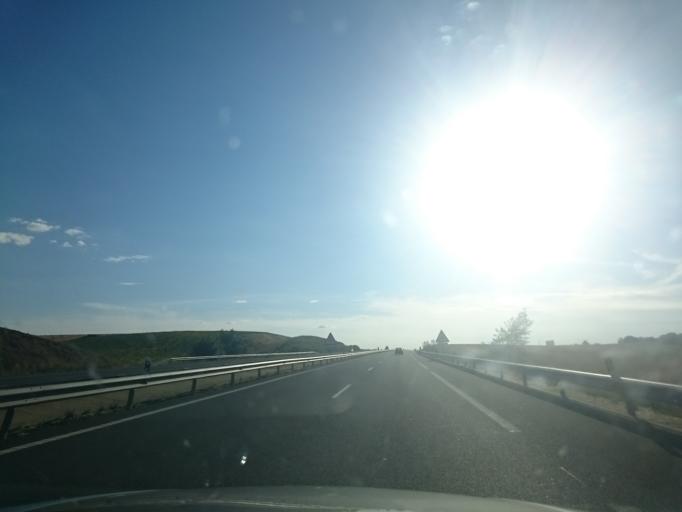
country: ES
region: Castille and Leon
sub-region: Provincia de Palencia
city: Osornillo
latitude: 42.4010
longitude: -4.3314
